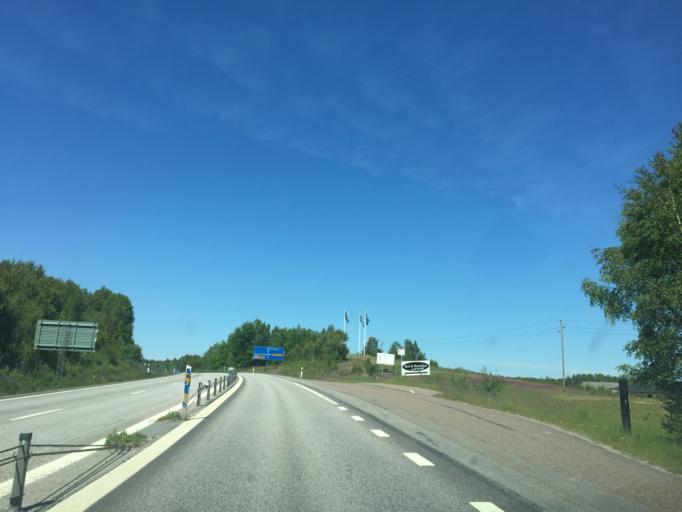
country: SE
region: OEstergoetland
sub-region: Motala Kommun
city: Motala
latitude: 58.6073
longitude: 14.9863
